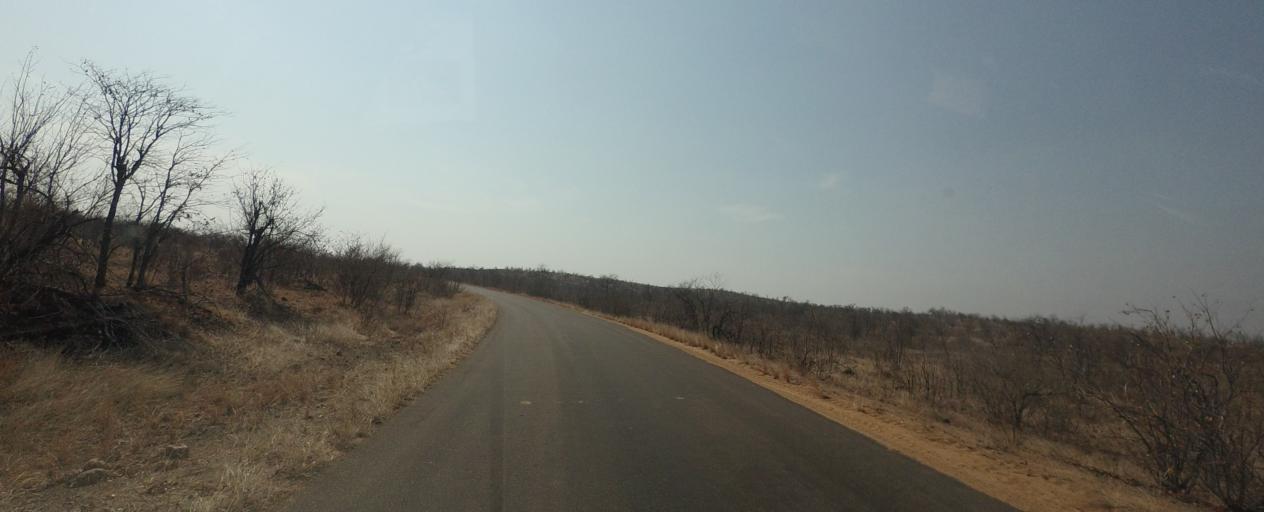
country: ZA
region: Limpopo
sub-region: Mopani District Municipality
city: Phalaborwa
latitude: -23.9721
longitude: 31.6343
